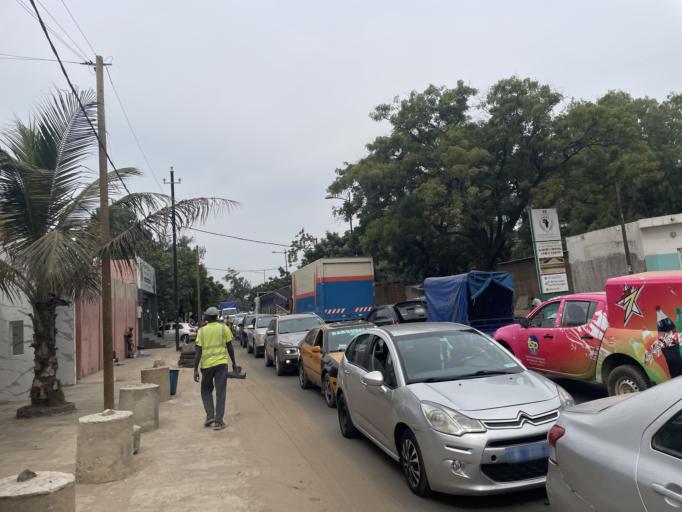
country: SN
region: Dakar
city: Grand Dakar
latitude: 14.7222
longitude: -17.4367
